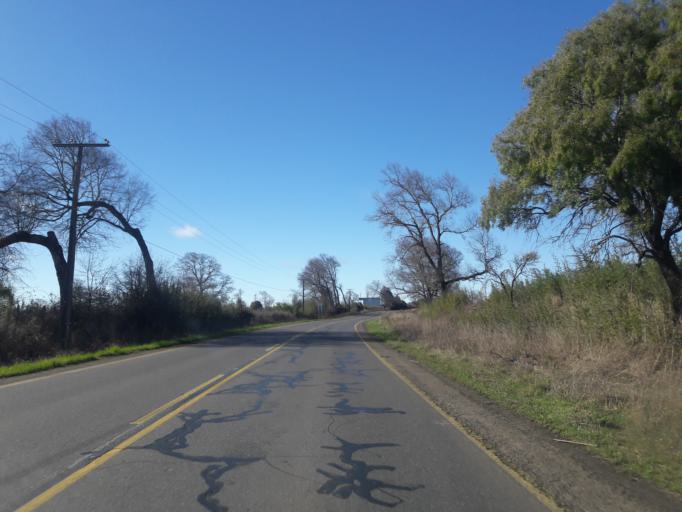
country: CL
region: Araucania
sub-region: Provincia de Malleco
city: Victoria
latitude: -38.2534
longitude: -72.2841
